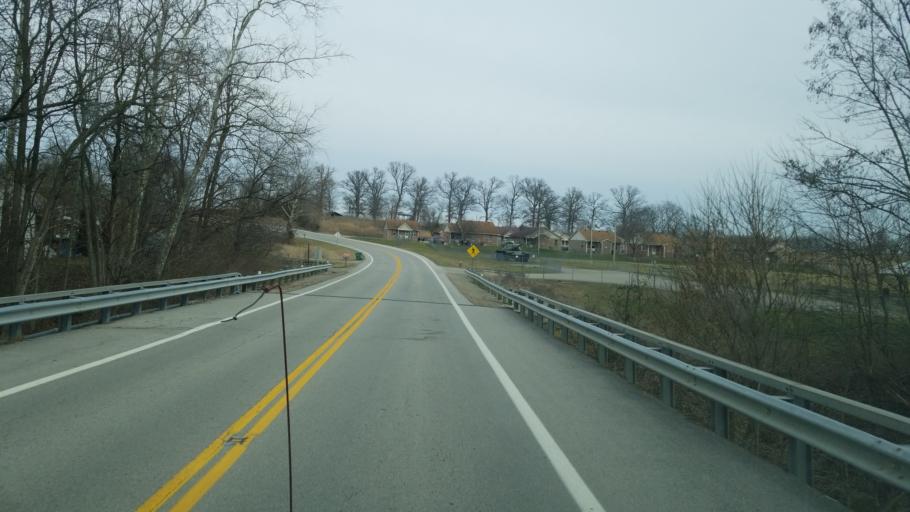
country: US
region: Ohio
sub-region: Pickaway County
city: Williamsport
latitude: 39.5062
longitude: -83.1512
